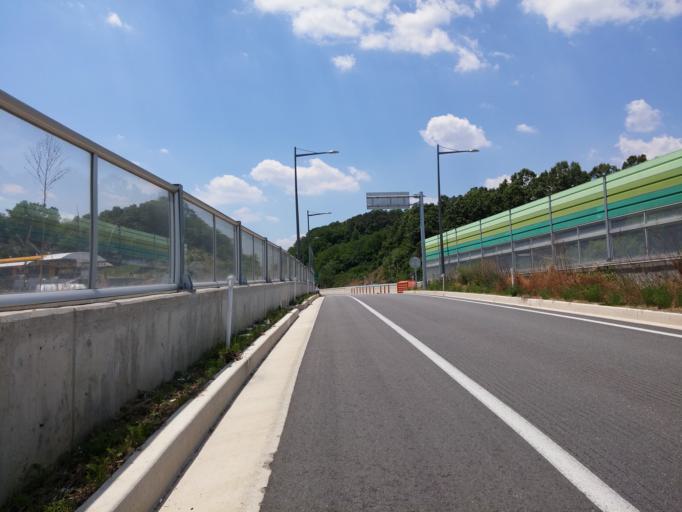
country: KR
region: Chungcheongbuk-do
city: Cheongju-si
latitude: 36.6032
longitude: 127.4385
